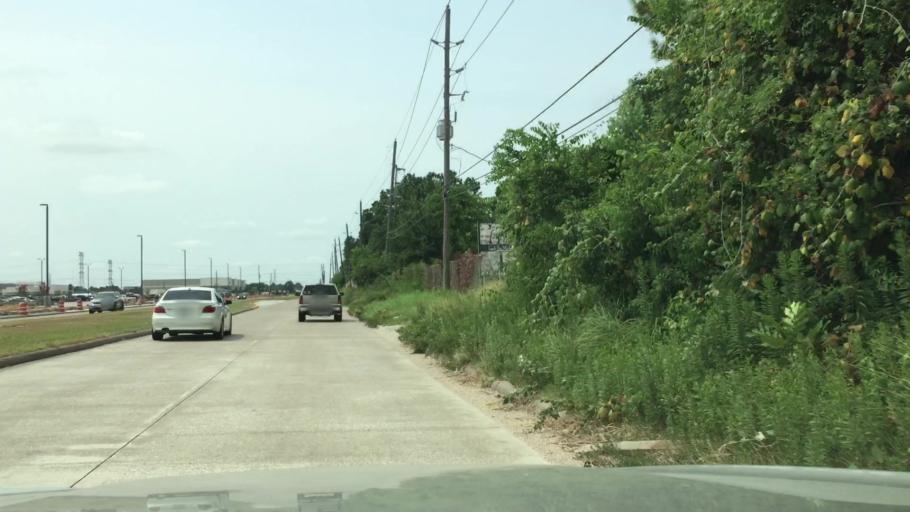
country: US
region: Texas
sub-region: Harris County
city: Jersey Village
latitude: 29.9464
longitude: -95.5470
